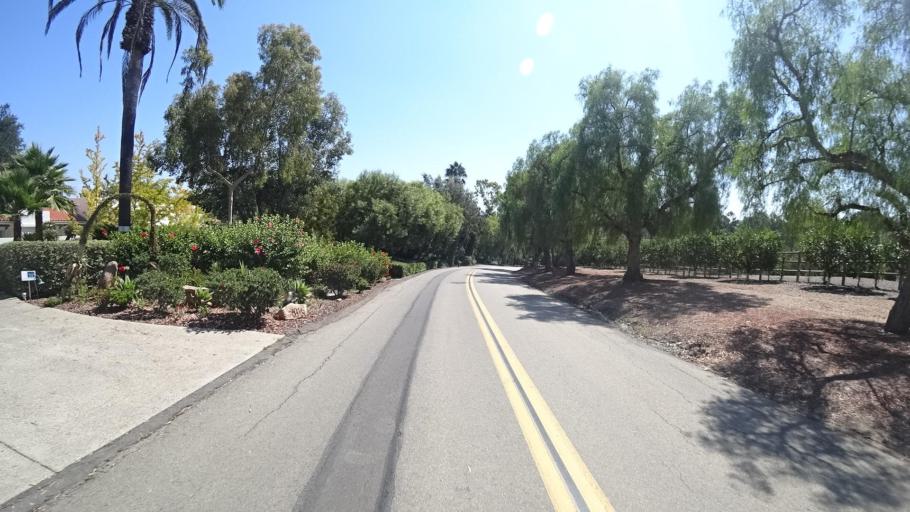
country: US
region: California
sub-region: San Diego County
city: Rancho Santa Fe
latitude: 33.0272
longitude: -117.1827
